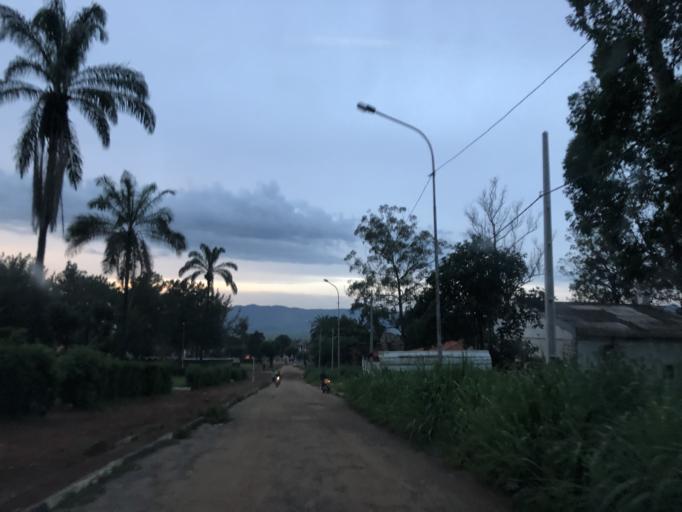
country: AO
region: Cuanza Sul
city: Uacu Cungo
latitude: -11.3675
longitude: 15.1174
